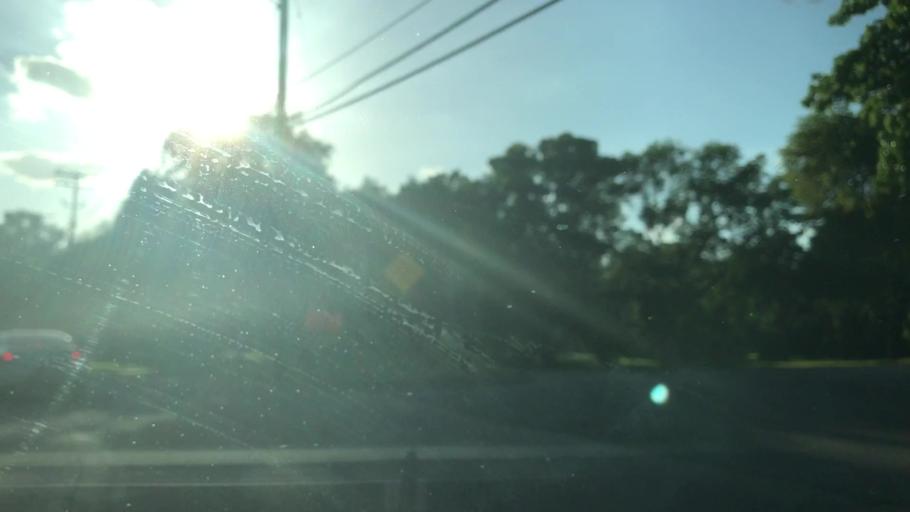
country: US
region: Texas
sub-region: Dallas County
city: Highland Park
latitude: 32.8197
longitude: -96.7993
